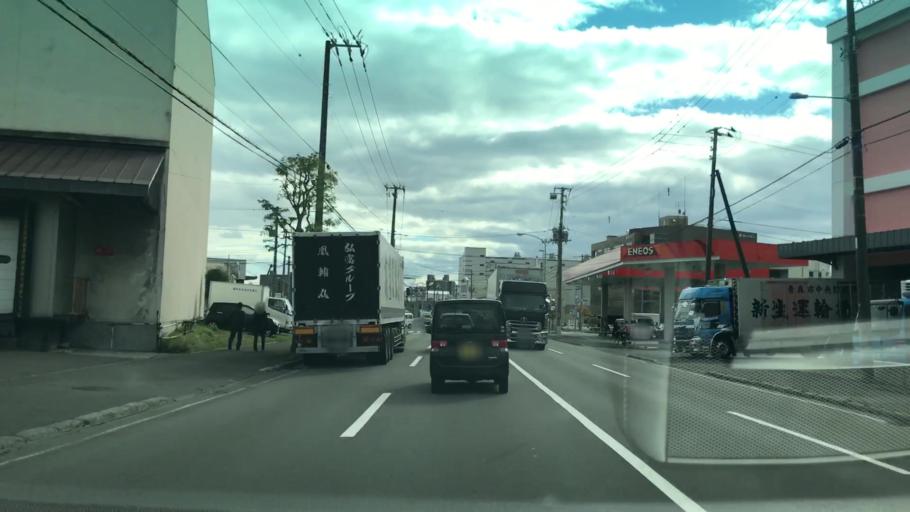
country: JP
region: Hokkaido
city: Sapporo
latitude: 43.0731
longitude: 141.3175
